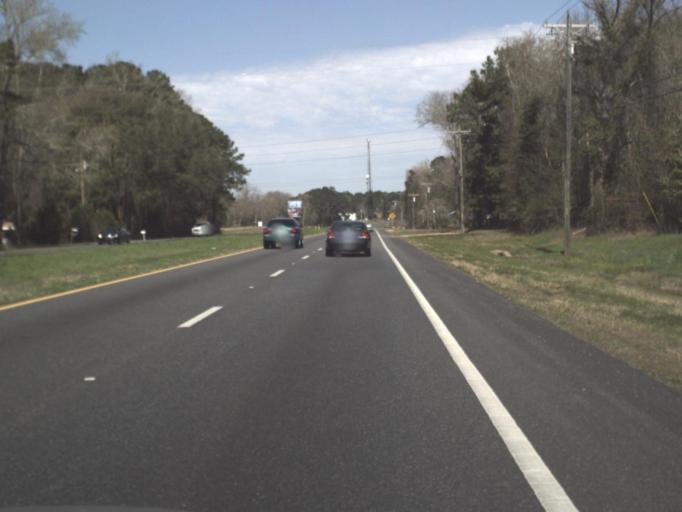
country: US
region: Florida
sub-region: Gadsden County
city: Havana
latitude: 30.6009
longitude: -84.4186
